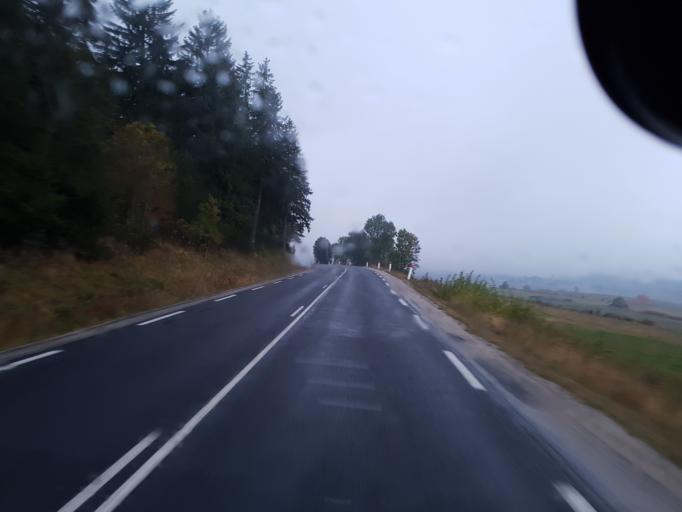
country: FR
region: Languedoc-Roussillon
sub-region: Departement de la Lozere
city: Langogne
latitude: 44.8204
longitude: 3.8722
